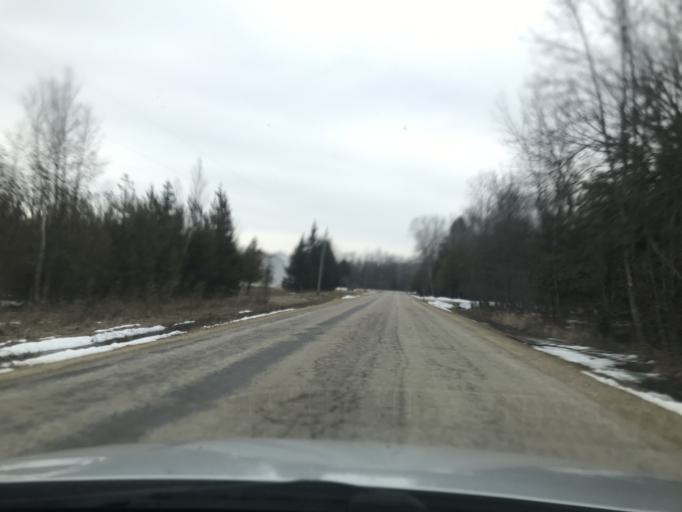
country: US
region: Wisconsin
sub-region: Marinette County
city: Peshtigo
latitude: 45.0883
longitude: -87.9324
